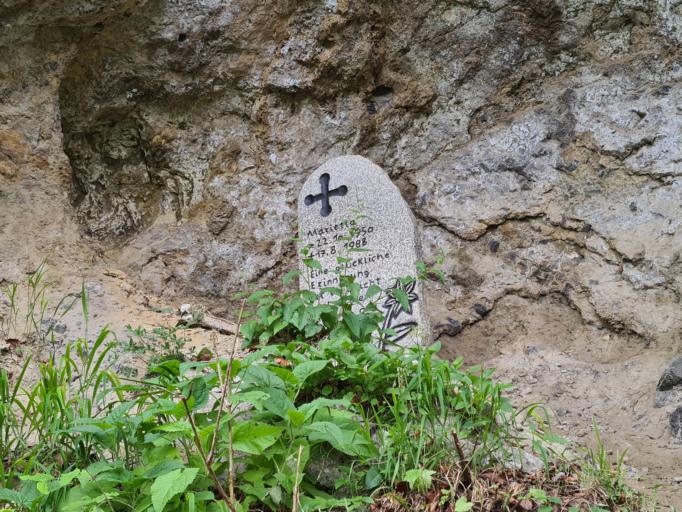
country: AT
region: Salzburg
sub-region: Politischer Bezirk Zell am See
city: Saalfelden am Steinernen Meer
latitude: 47.4431
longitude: 12.8604
